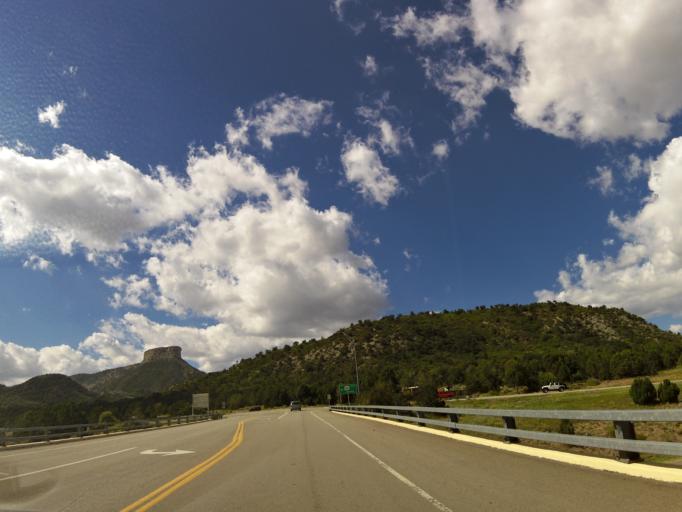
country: US
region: Colorado
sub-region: Montezuma County
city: Mancos
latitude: 37.3410
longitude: -108.4113
